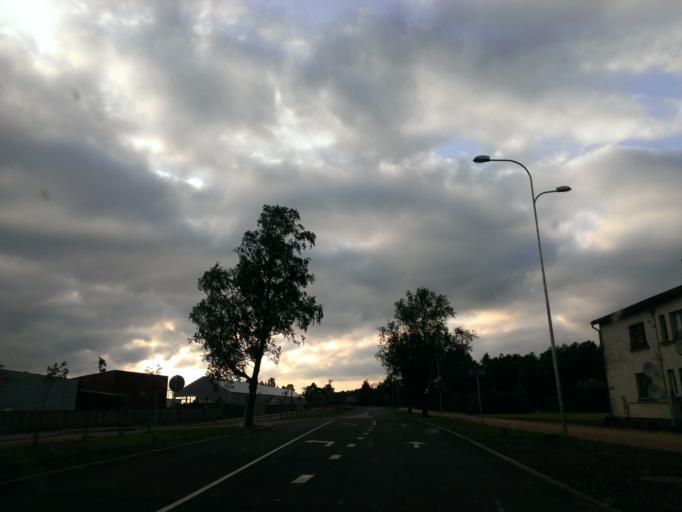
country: LV
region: Saldus Rajons
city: Saldus
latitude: 56.6830
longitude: 22.4718
